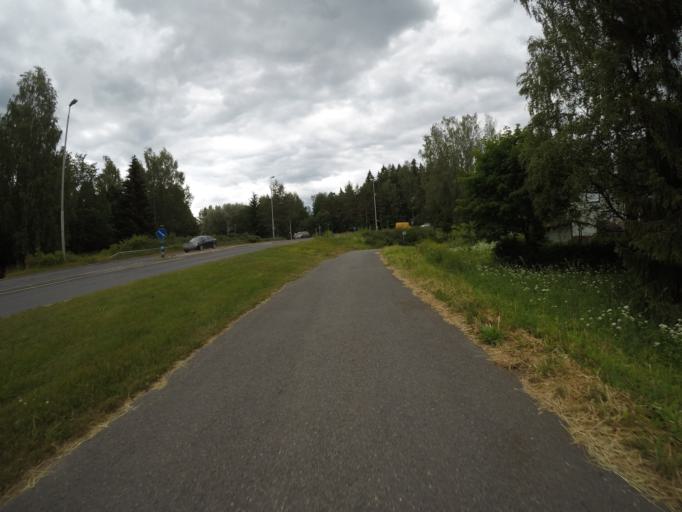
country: FI
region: Haeme
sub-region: Haemeenlinna
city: Haemeenlinna
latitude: 60.9886
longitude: 24.4316
